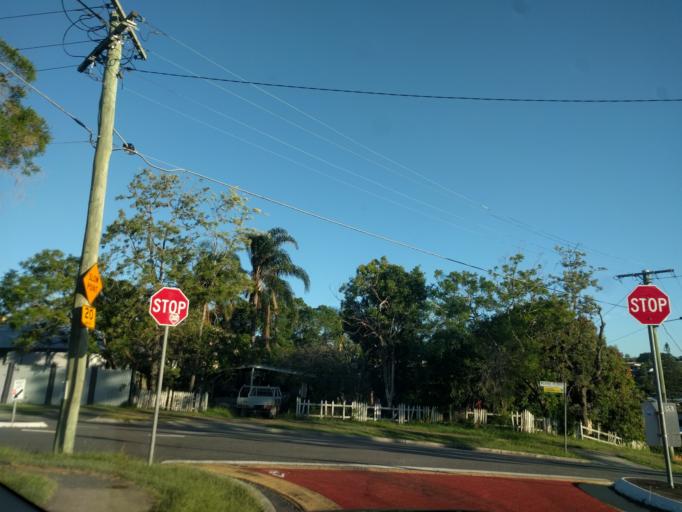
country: AU
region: Queensland
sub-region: Brisbane
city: Annerley
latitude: -27.5043
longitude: 153.0290
